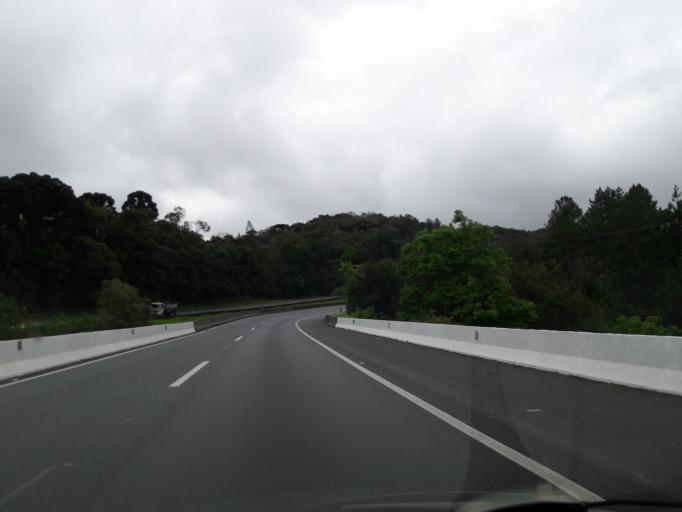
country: BR
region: Parana
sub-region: Campina Grande Do Sul
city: Campina Grande do Sul
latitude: -25.2031
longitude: -48.8957
